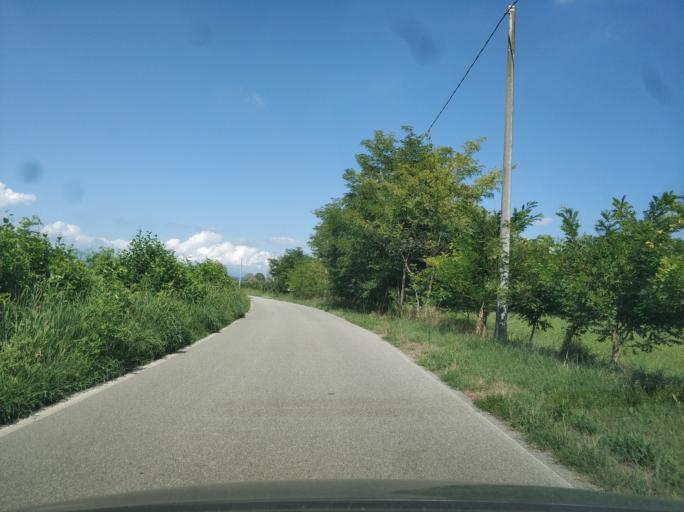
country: IT
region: Piedmont
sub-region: Provincia di Torino
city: Feletto
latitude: 45.2995
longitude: 7.7226
